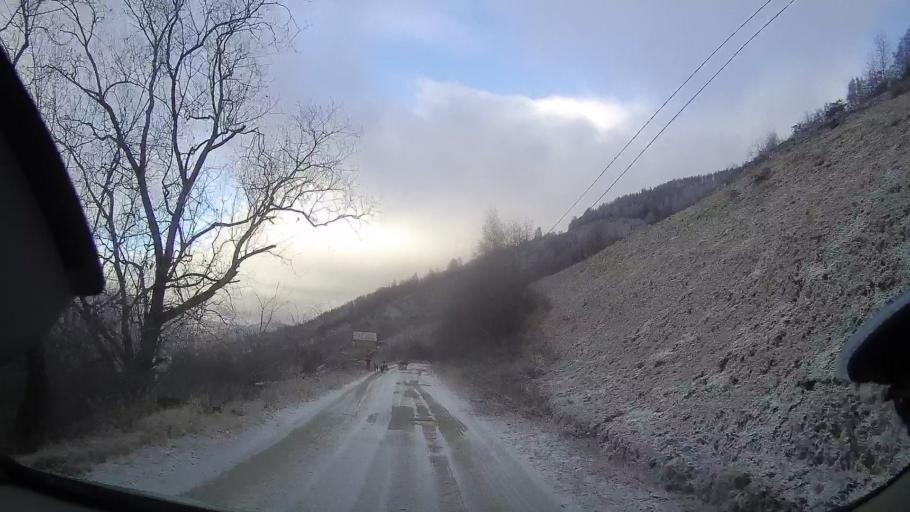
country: RO
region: Cluj
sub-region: Comuna Valea Ierii
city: Valea Ierii
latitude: 46.6676
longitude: 23.3316
